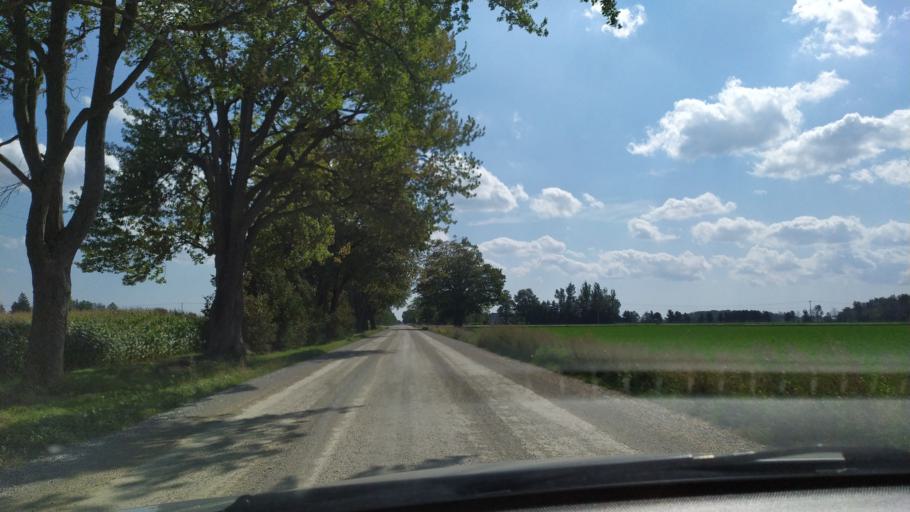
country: CA
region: Ontario
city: Stratford
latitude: 43.2657
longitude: -80.9192
